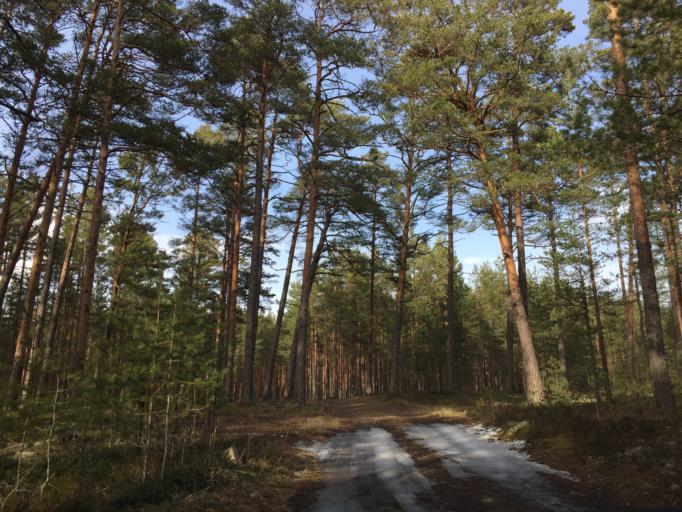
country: EE
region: Paernumaa
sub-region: Paernu linn
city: Parnu
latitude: 58.2315
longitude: 24.5166
